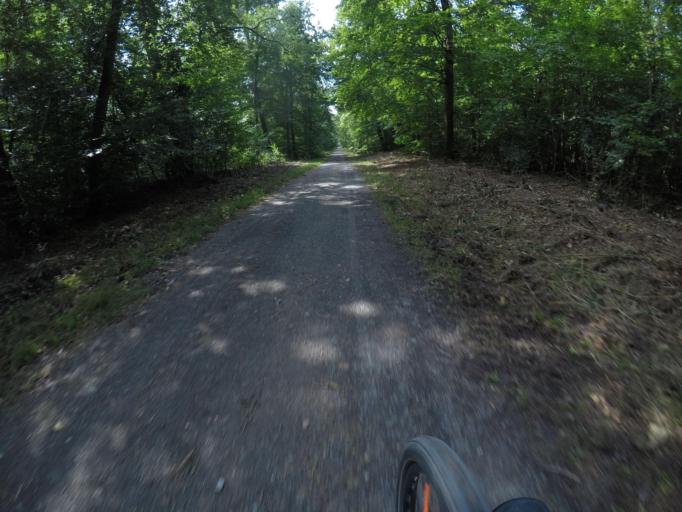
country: DE
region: Baden-Wuerttemberg
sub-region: Karlsruhe Region
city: Reilingen
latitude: 49.2787
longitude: 8.5692
